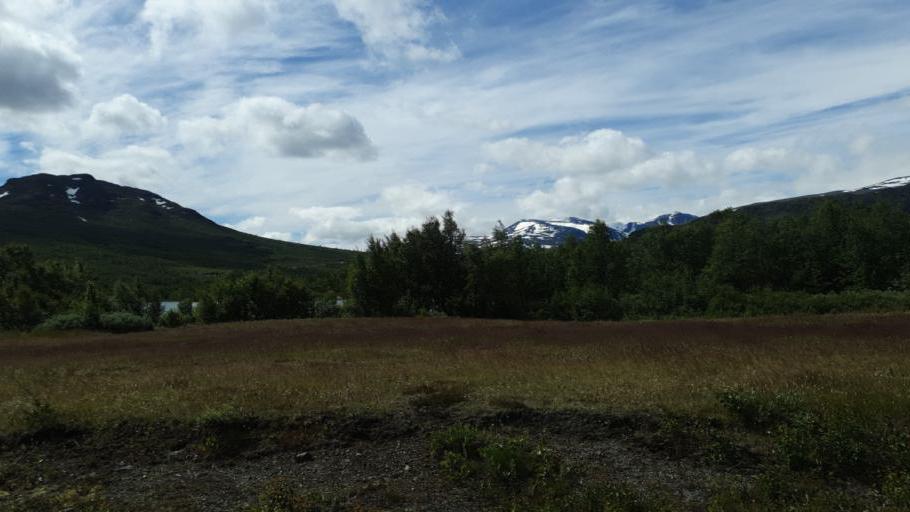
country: NO
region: Oppland
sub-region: Oystre Slidre
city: Heggenes
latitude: 61.4888
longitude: 8.8264
